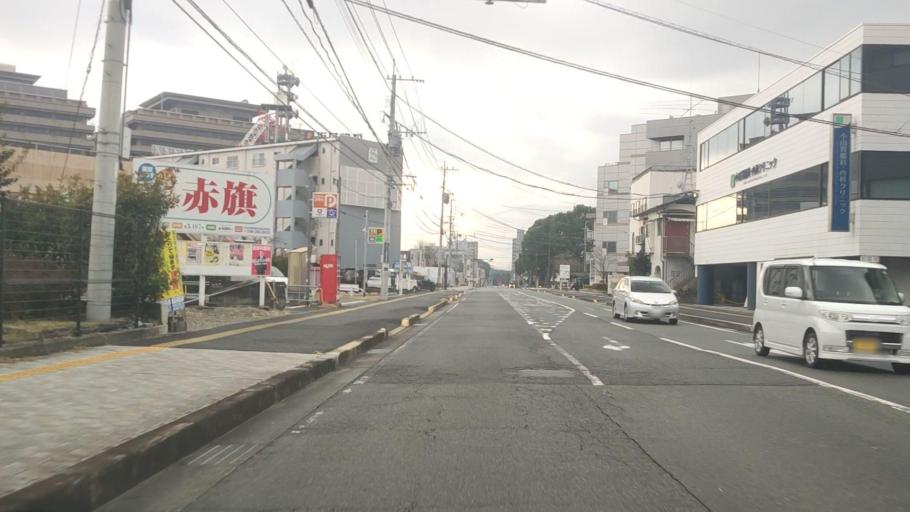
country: JP
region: Kumamoto
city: Kumamoto
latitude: 32.7927
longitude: 130.7412
